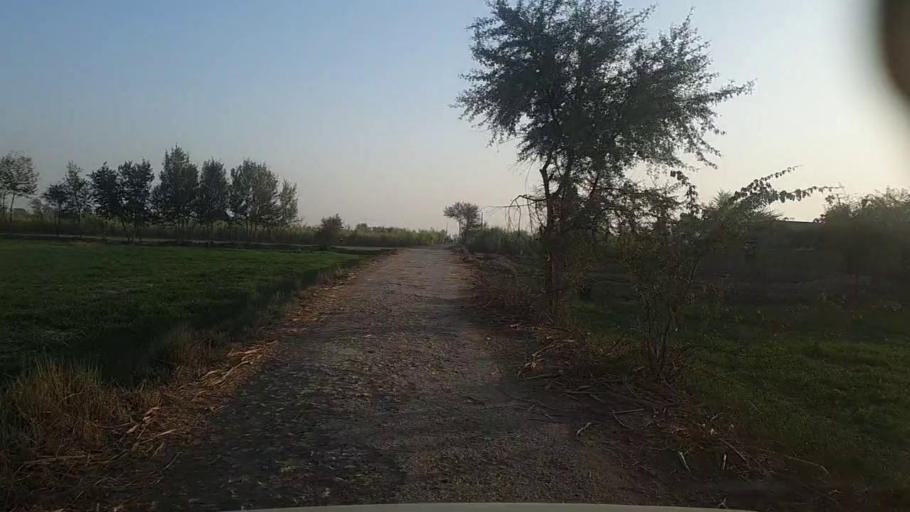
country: PK
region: Sindh
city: Khairpur
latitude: 28.0600
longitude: 69.7576
